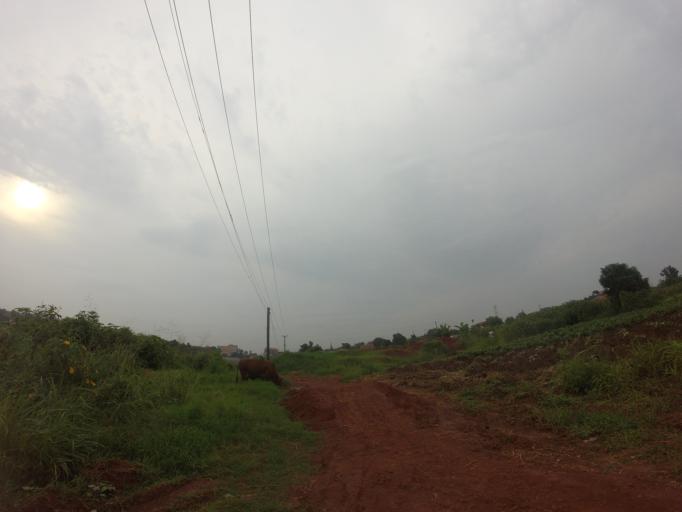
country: UG
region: Central Region
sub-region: Wakiso District
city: Kireka
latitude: 0.3558
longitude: 32.6238
